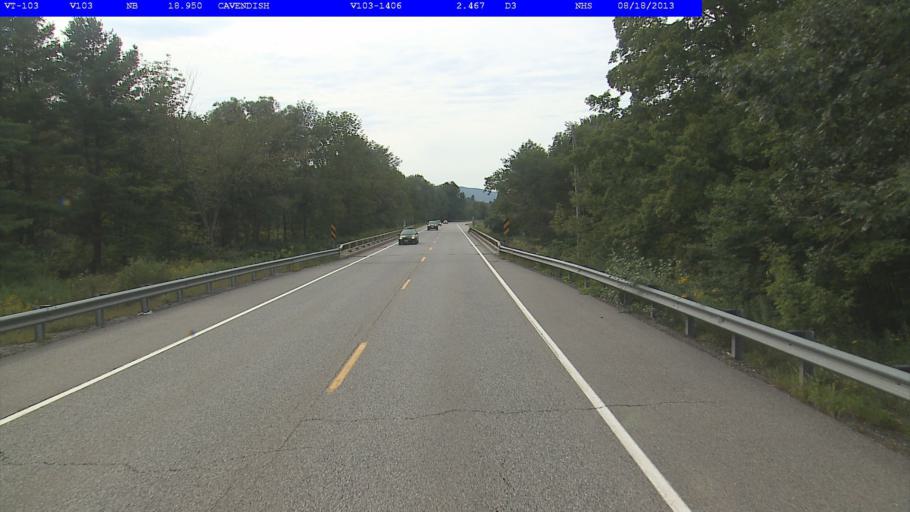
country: US
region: Vermont
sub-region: Windsor County
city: Chester
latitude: 43.3793
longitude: -72.6413
